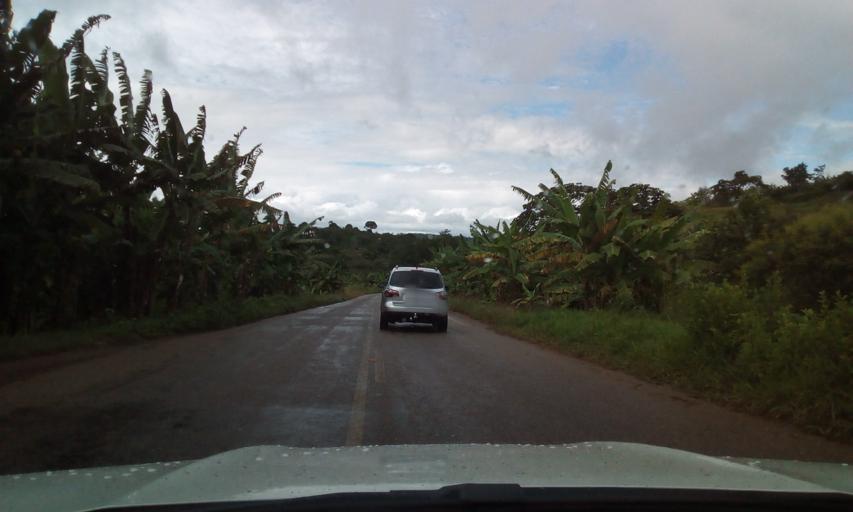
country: BR
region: Paraiba
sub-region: Areia
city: Areia
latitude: -6.9176
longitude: -35.6423
